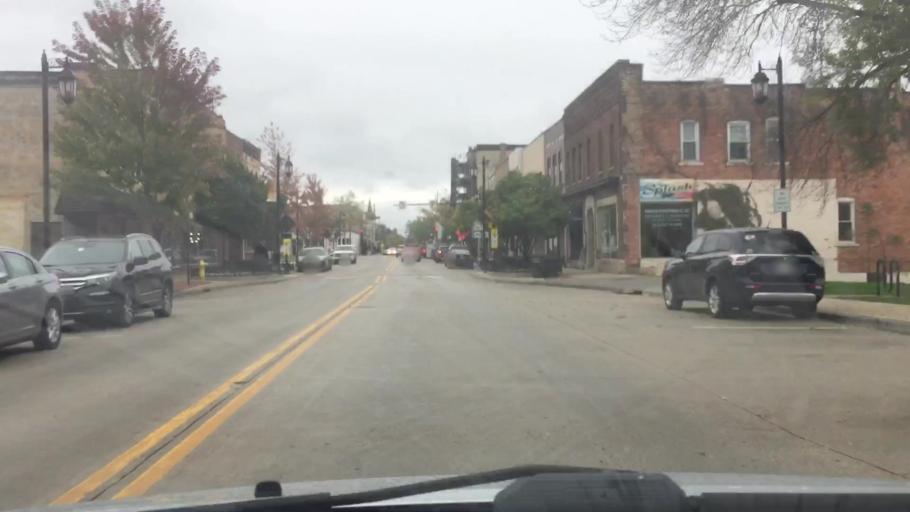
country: US
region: Wisconsin
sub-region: Waukesha County
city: Oconomowoc
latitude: 43.1128
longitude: -88.4996
